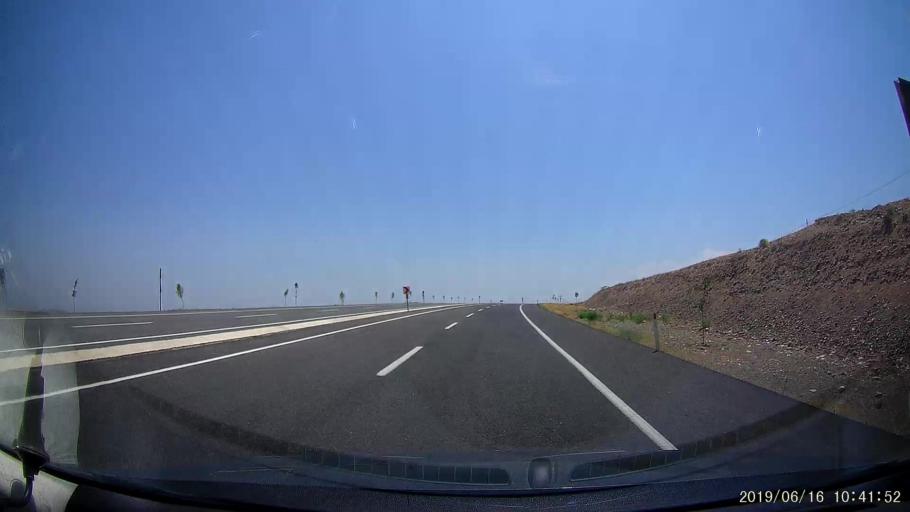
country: AM
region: Armavir
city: Shenavan
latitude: 40.0457
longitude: 43.7947
